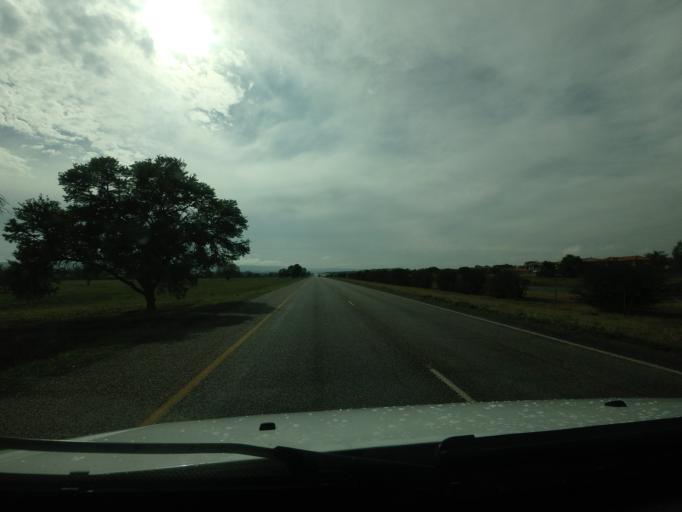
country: ZA
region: Gauteng
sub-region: City of Tshwane Metropolitan Municipality
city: Pretoria
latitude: -25.7602
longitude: 28.3644
